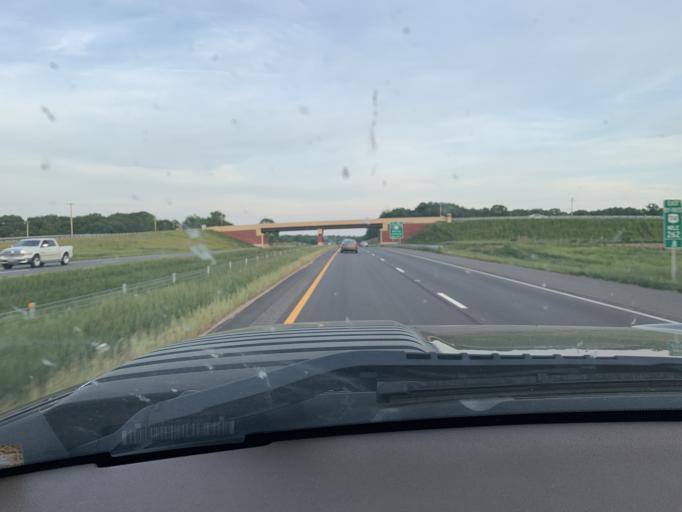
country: US
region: North Carolina
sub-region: Union County
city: Monroe
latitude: 35.0448
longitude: -80.5678
